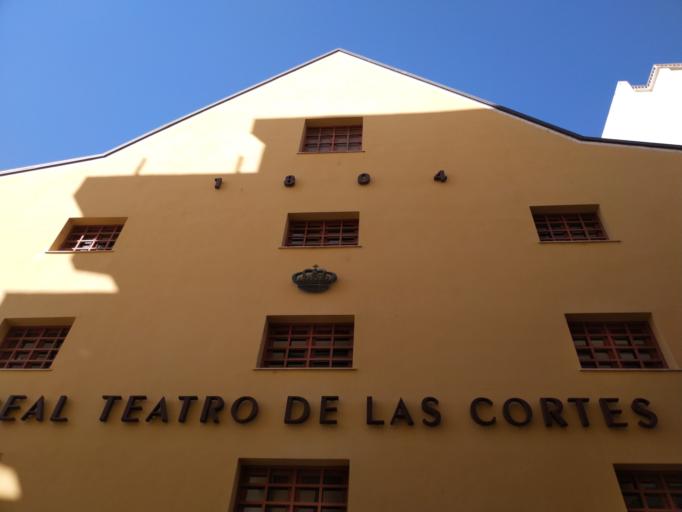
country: ES
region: Andalusia
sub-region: Provincia de Cadiz
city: San Fernando
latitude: 36.4661
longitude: -6.1975
